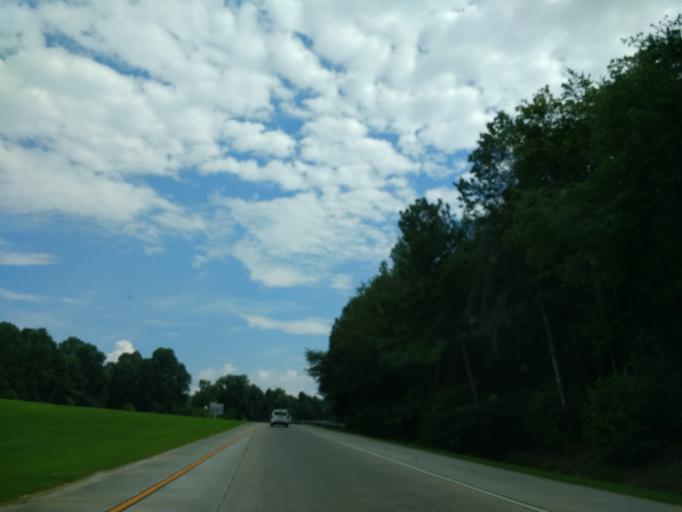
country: US
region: Georgia
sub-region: Hall County
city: Gainesville
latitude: 34.3139
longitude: -83.7888
